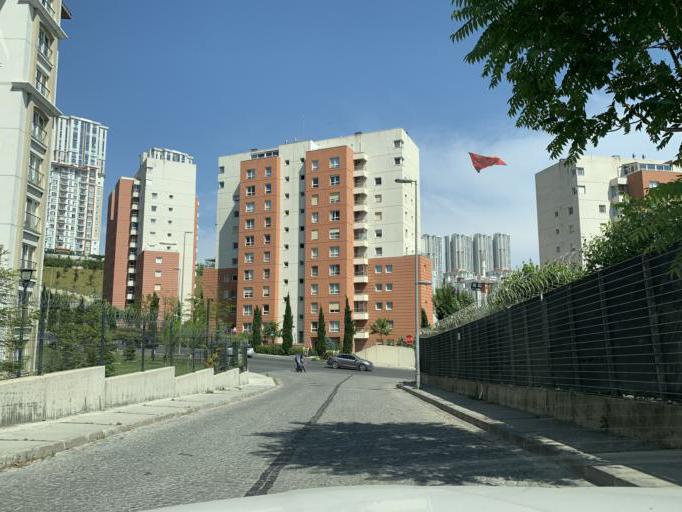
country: TR
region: Istanbul
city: Esenyurt
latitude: 41.0790
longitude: 28.6903
